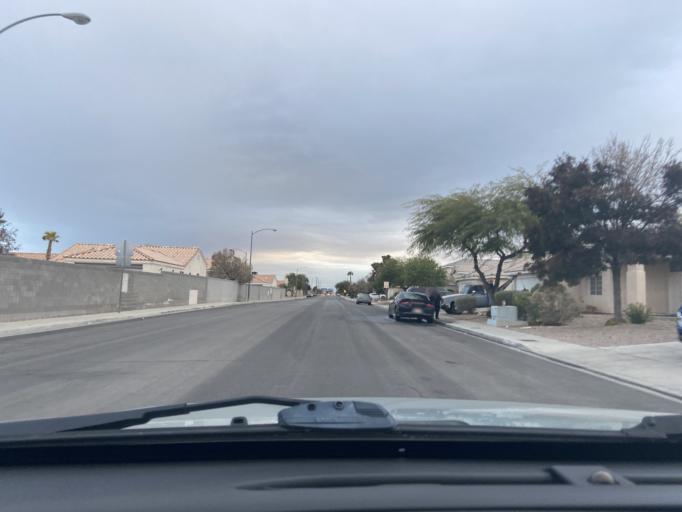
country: US
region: Nevada
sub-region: Clark County
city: Las Vegas
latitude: 36.2279
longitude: -115.1845
